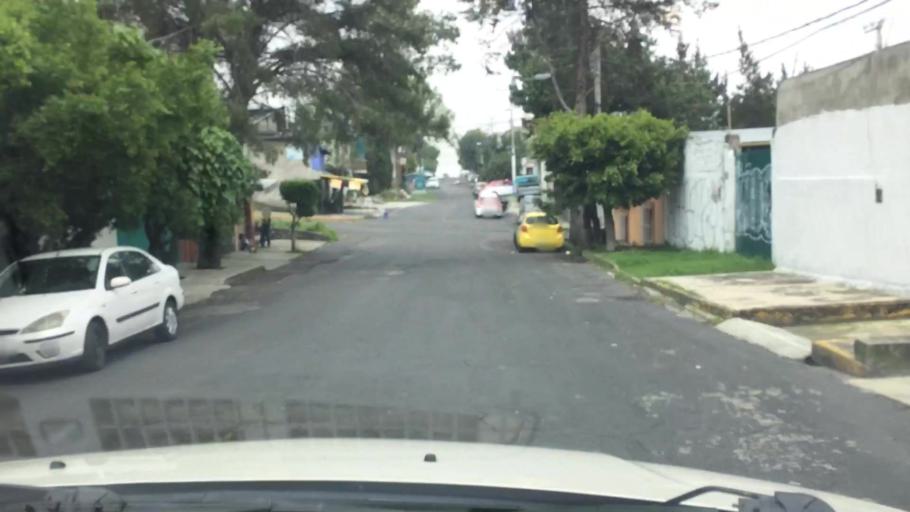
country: MX
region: Mexico City
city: Magdalena Contreras
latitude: 19.2914
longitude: -99.2249
